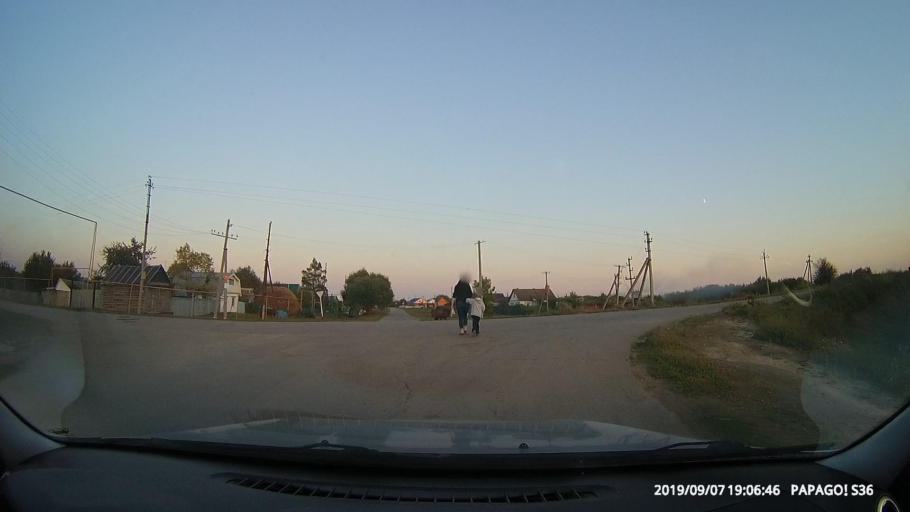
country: RU
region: Samara
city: Chapayevsk
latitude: 52.9919
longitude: 49.7765
